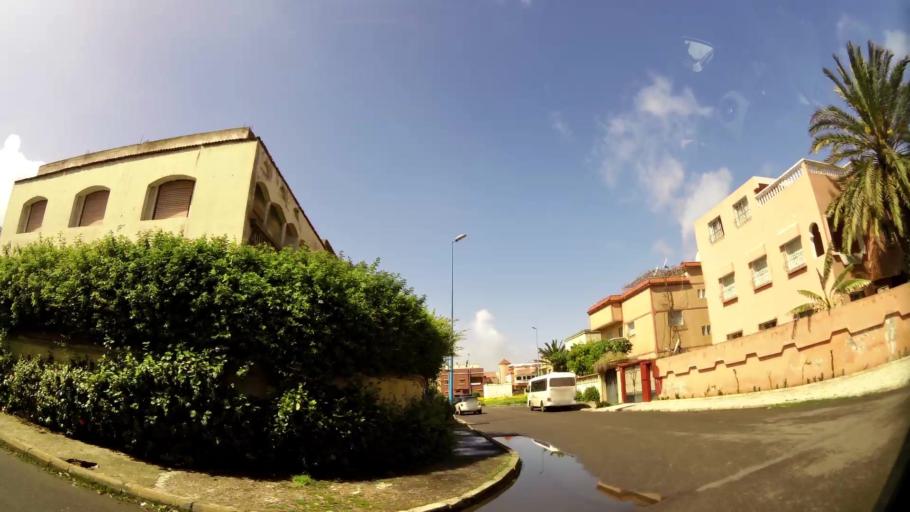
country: MA
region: Grand Casablanca
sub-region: Mediouna
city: Tit Mellil
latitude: 33.6187
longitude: -7.5231
